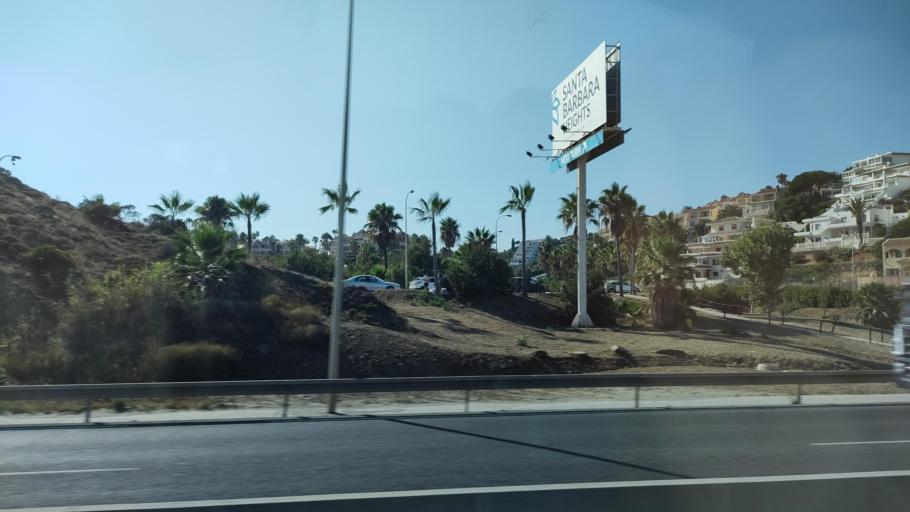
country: ES
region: Andalusia
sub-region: Provincia de Malaga
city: Fuengirola
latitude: 36.5136
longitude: -4.6342
